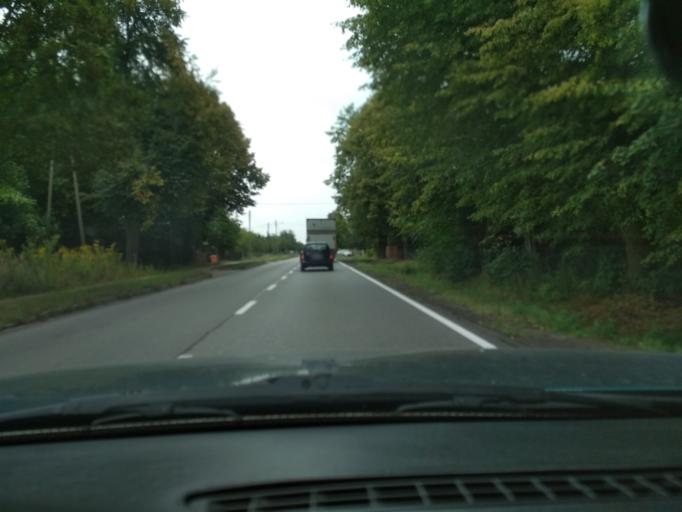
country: PL
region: Silesian Voivodeship
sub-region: Powiat zawiercianski
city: Wysoka
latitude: 50.4433
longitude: 19.3593
